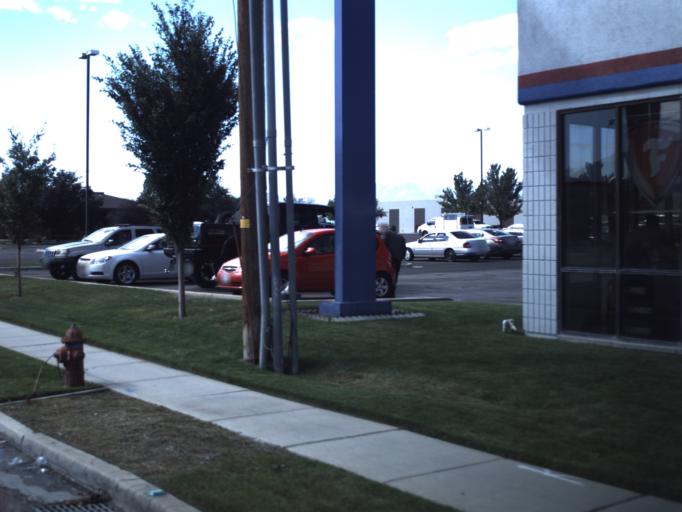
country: US
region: Utah
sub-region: Salt Lake County
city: West Jordan
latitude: 40.5870
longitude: -111.9388
